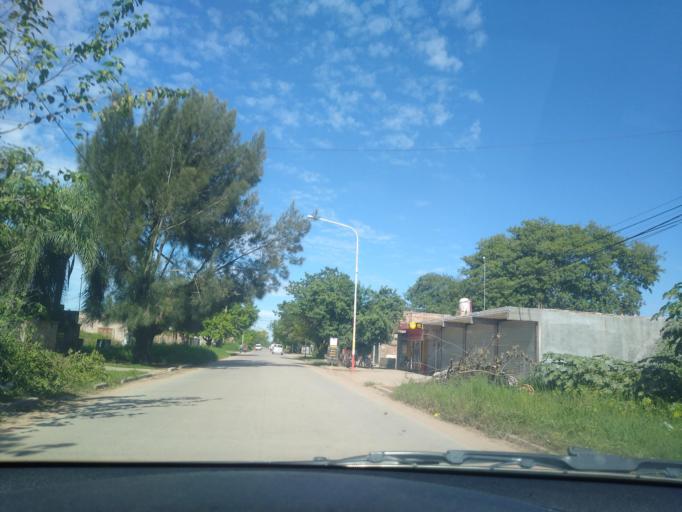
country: AR
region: Chaco
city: Presidencia Roque Saenz Pena
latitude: -26.7754
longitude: -60.4244
